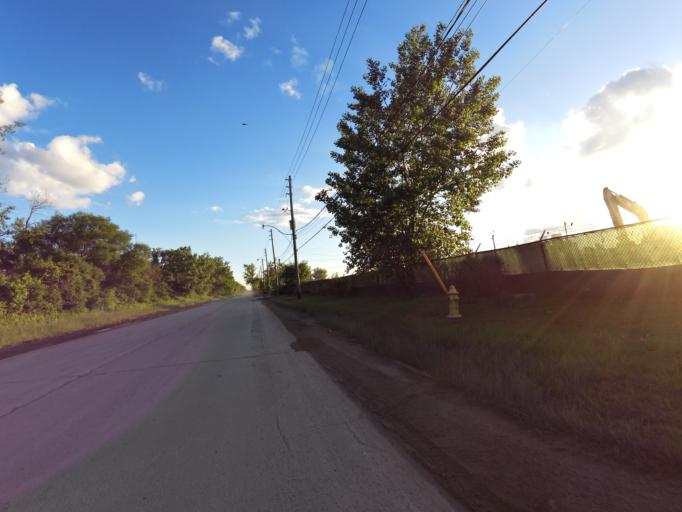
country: CA
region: Ontario
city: Toronto
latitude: 43.6438
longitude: -79.3384
